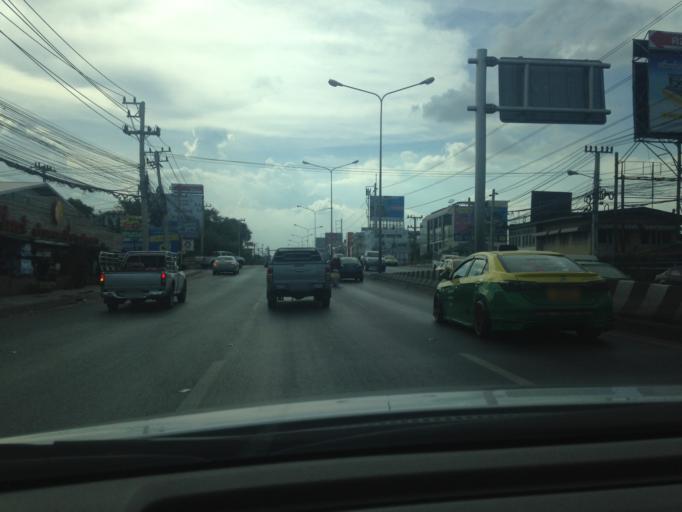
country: TH
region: Pathum Thani
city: Khlong Luang
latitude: 14.0654
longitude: 100.6429
